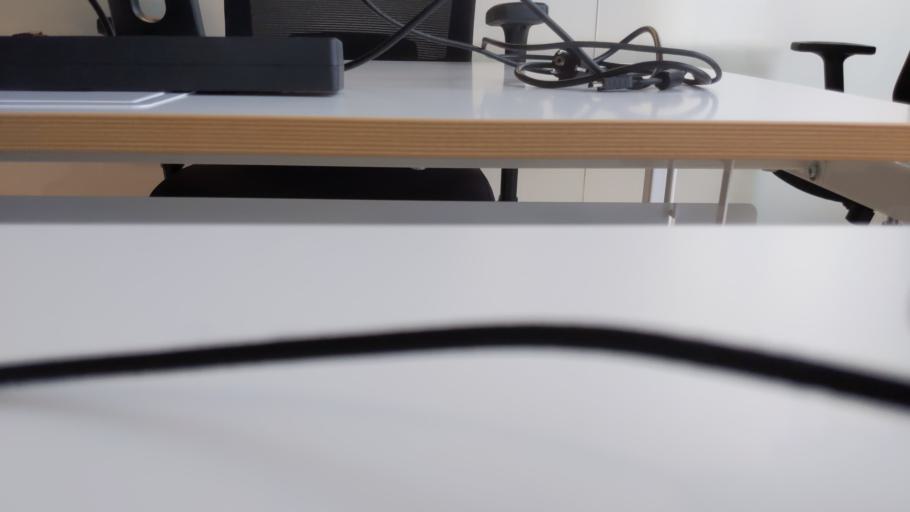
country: RU
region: Moskovskaya
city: Shevlyakovo
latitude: 56.4214
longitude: 37.0060
